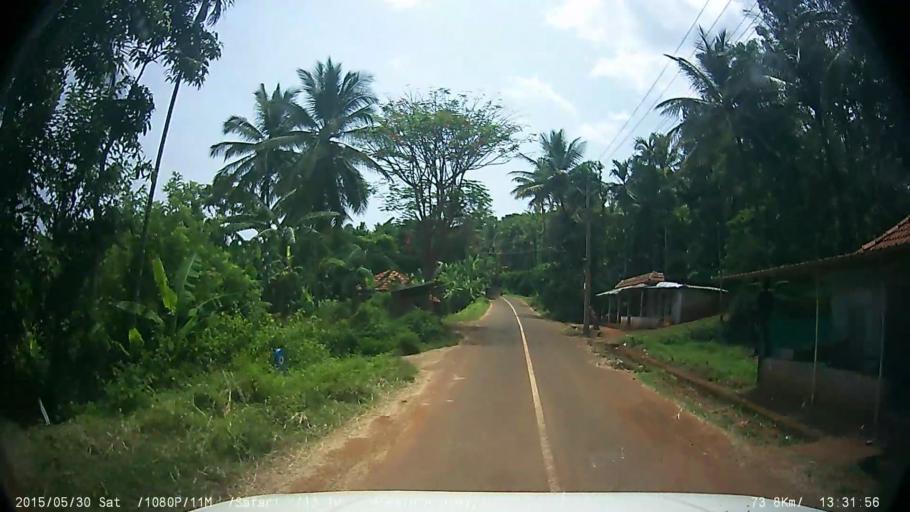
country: IN
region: Kerala
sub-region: Wayanad
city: Panamaram
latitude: 11.8170
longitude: 76.0811
